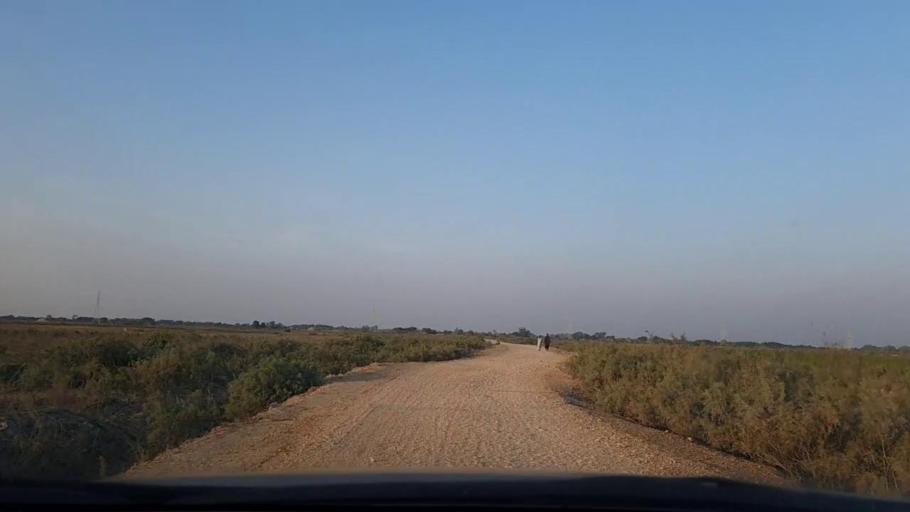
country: PK
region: Sindh
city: Mirpur Sakro
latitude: 24.5556
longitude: 67.6571
